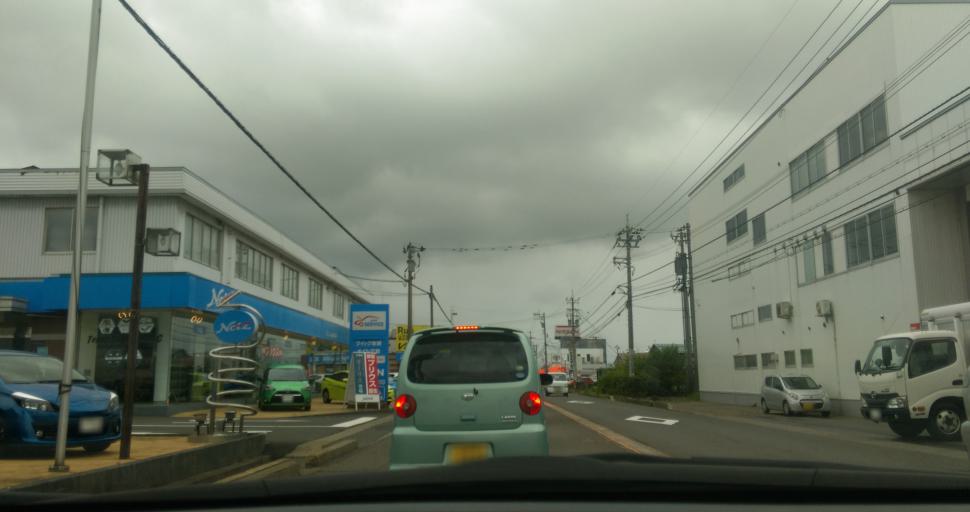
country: JP
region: Fukui
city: Fukui-shi
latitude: 36.0193
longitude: 136.2071
